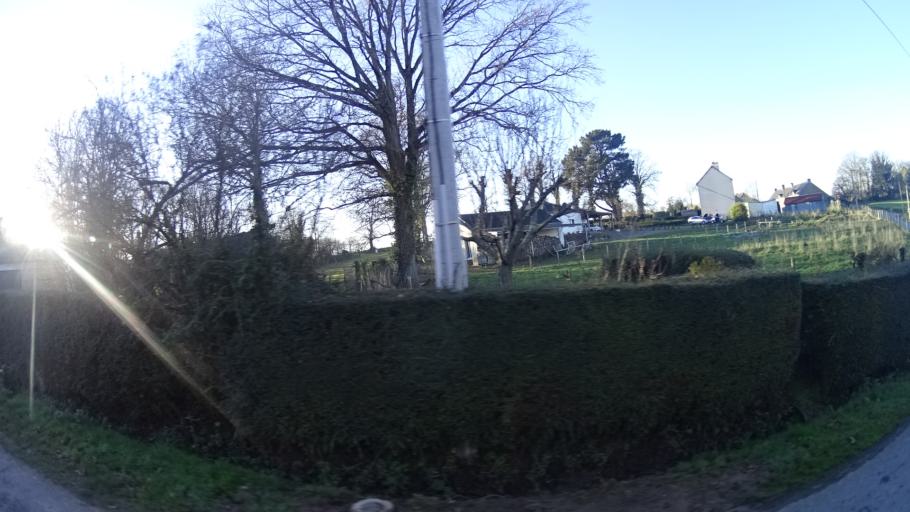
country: FR
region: Brittany
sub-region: Departement du Morbihan
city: Saint-Jean-la-Poterie
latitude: 47.6516
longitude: -2.1367
